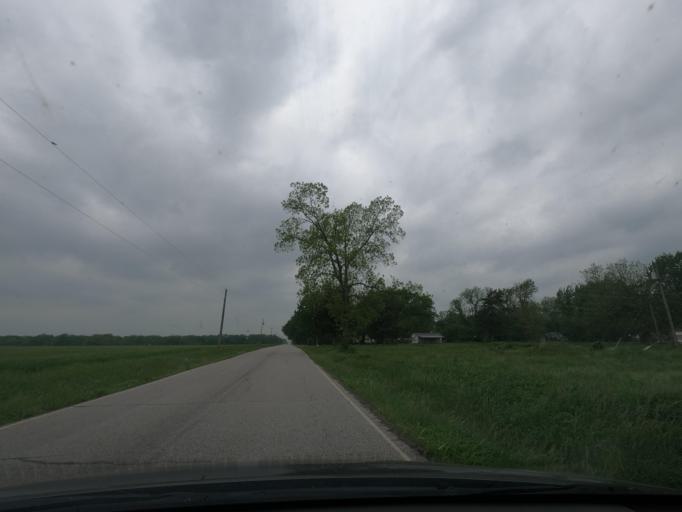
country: US
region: Kansas
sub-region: Cherokee County
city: Columbus
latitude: 37.2817
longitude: -94.9259
